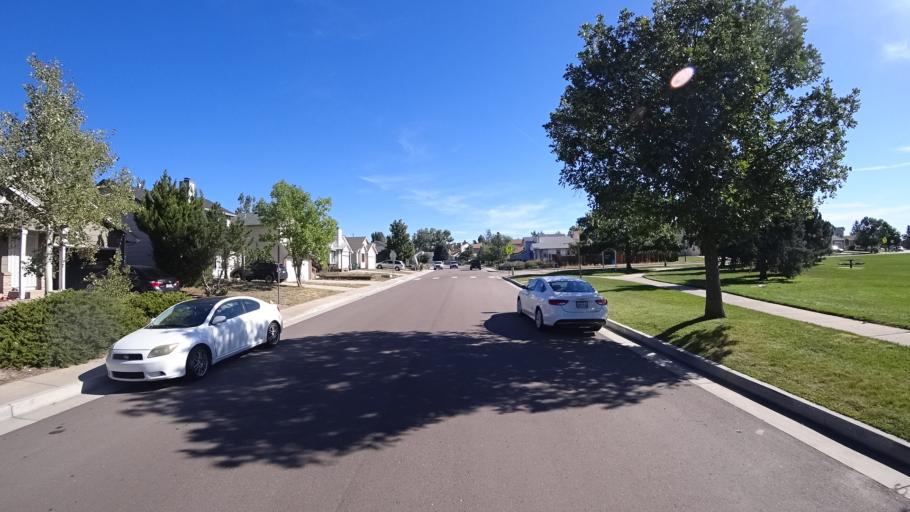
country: US
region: Colorado
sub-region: El Paso County
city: Black Forest
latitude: 38.9503
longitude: -104.7378
